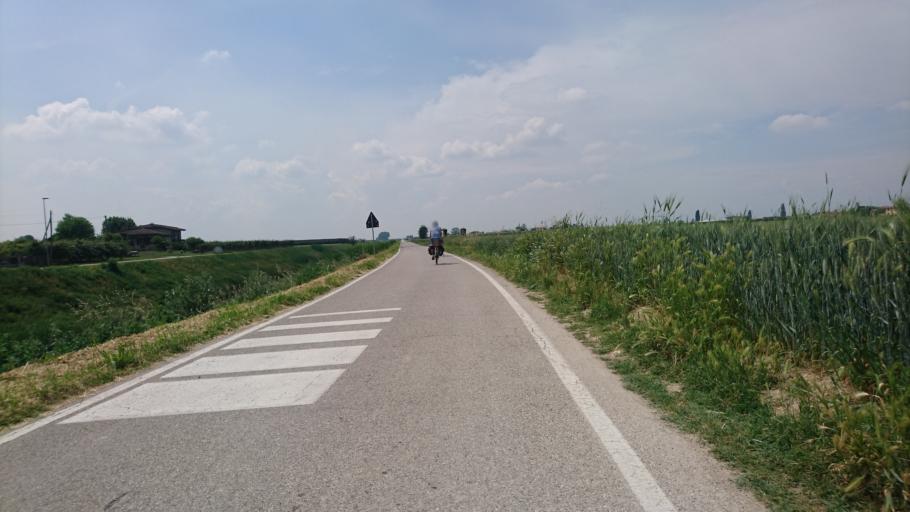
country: IT
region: Veneto
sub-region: Provincia di Rovigo
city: Giacciano con Baruchella
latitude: 45.0690
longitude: 11.4483
